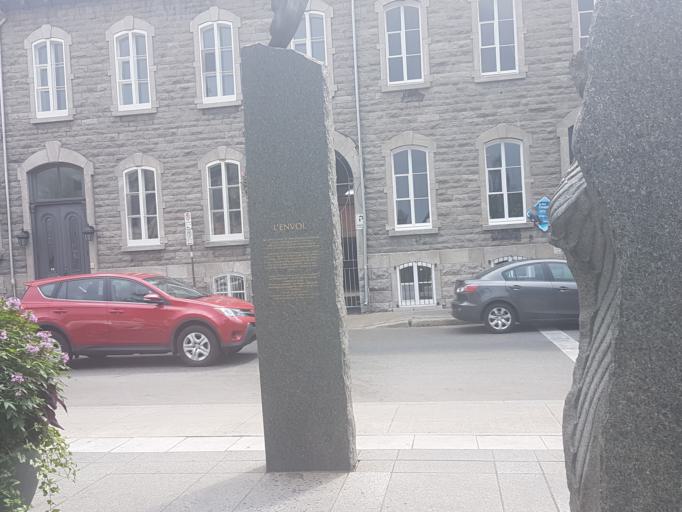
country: CA
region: Quebec
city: Quebec
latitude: 46.8132
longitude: -71.2087
